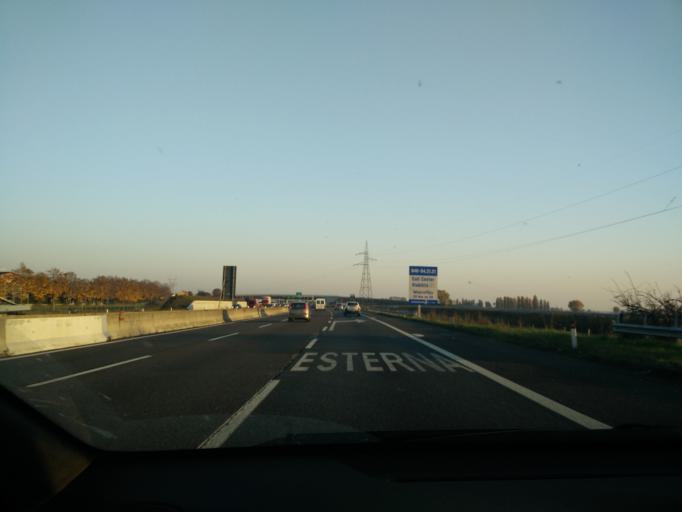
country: IT
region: Lombardy
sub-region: Citta metropolitana di Milano
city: Riozzo
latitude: 45.3445
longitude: 9.3152
